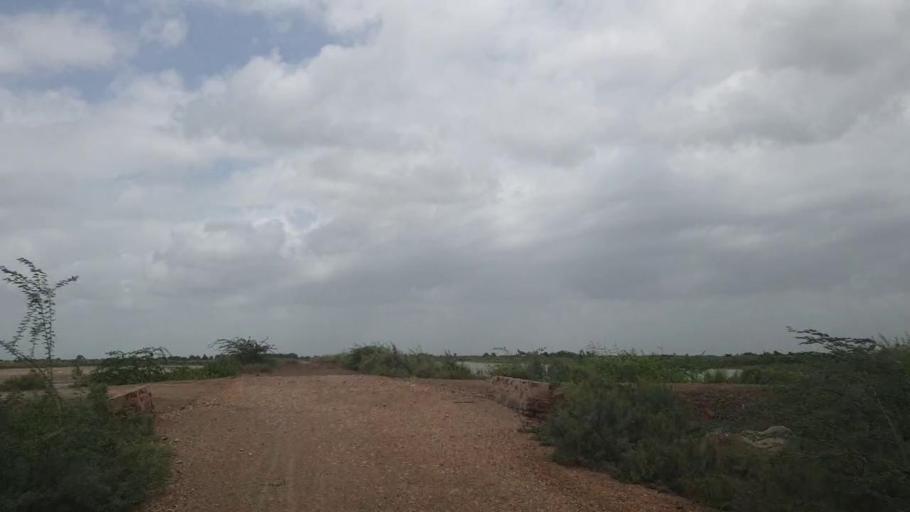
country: PK
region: Sindh
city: Badin
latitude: 24.6267
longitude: 68.9509
